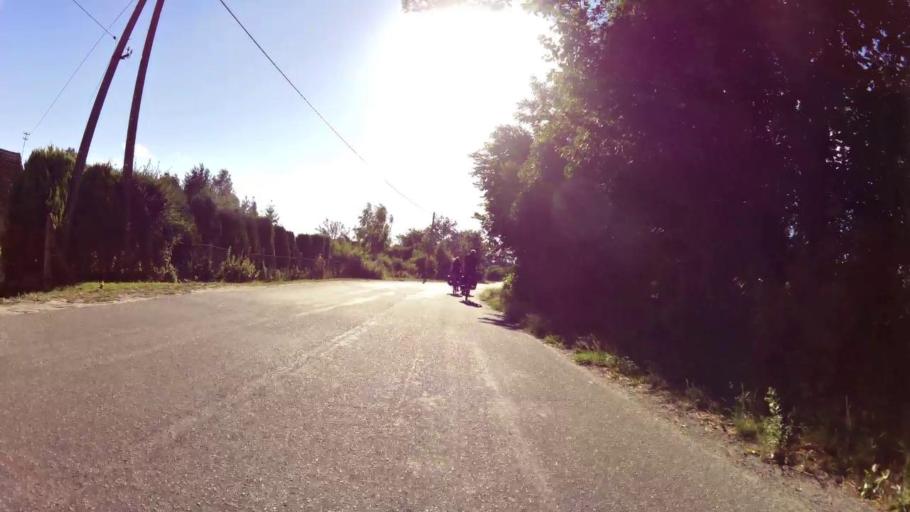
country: PL
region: West Pomeranian Voivodeship
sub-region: Powiat swidwinski
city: Swidwin
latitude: 53.7752
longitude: 15.7458
